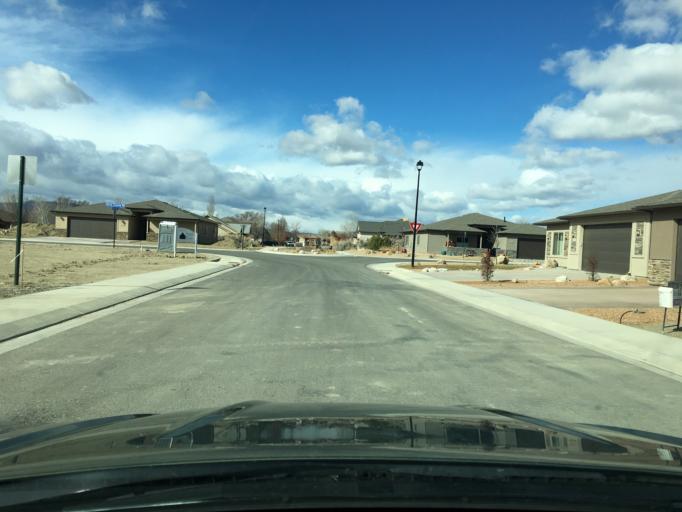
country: US
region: Colorado
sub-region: Mesa County
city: Grand Junction
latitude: 39.1324
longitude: -108.5556
